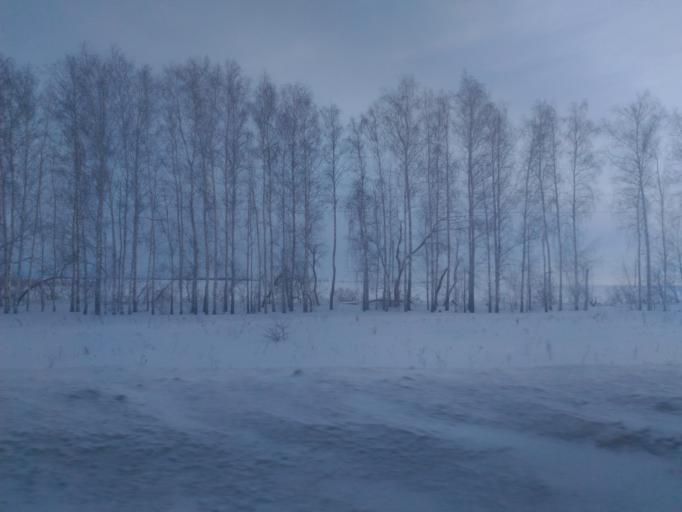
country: RU
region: Ulyanovsk
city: Isheyevka
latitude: 54.4110
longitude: 48.2951
